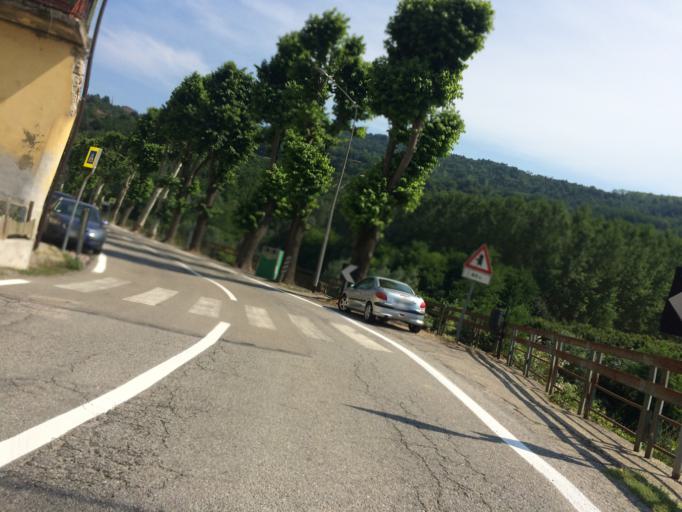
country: IT
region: Piedmont
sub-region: Provincia di Cuneo
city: Cortemilia
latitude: 44.5788
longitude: 8.1872
